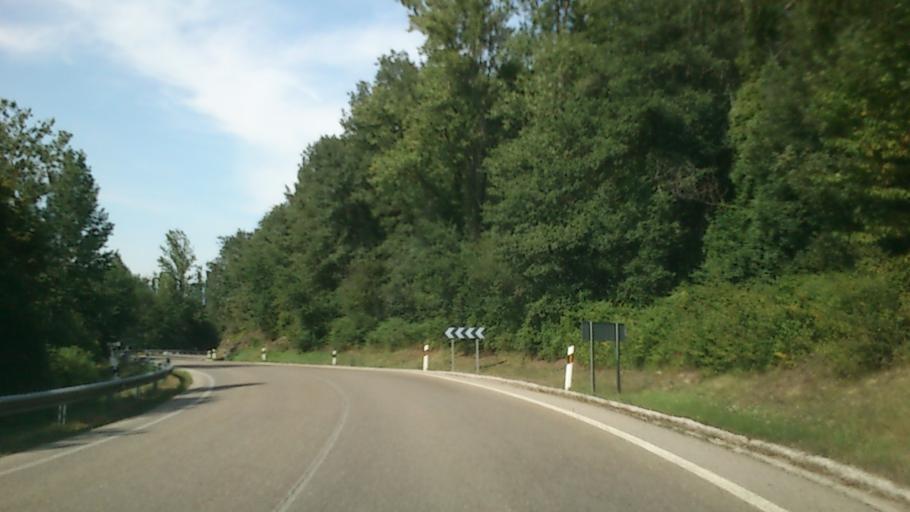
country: ES
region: Castille and Leon
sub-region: Provincia de Burgos
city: Medina de Pomar
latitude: 43.0193
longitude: -3.4833
